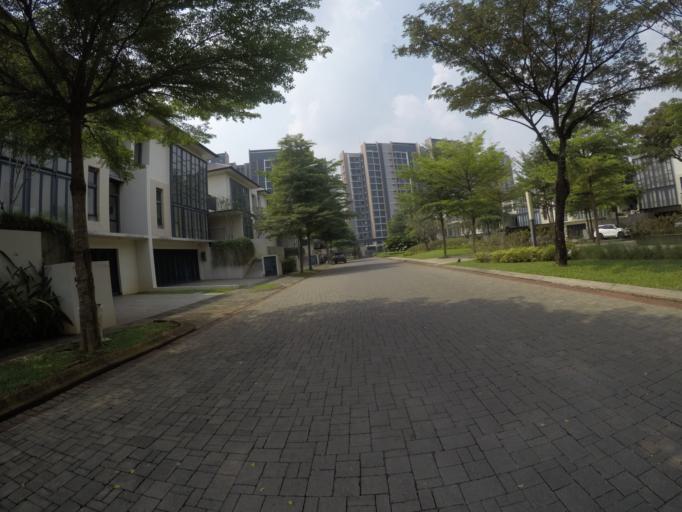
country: ID
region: West Java
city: Serpong
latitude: -6.2968
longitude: 106.6492
